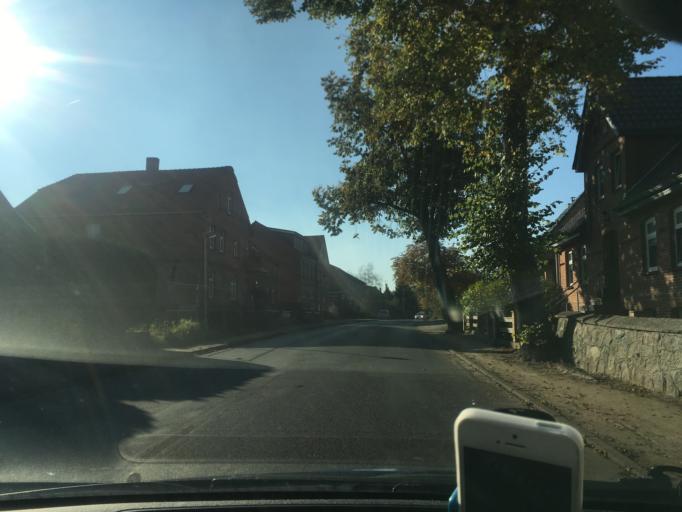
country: DE
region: Mecklenburg-Vorpommern
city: Stralendorf
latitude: 53.5752
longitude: 11.3052
